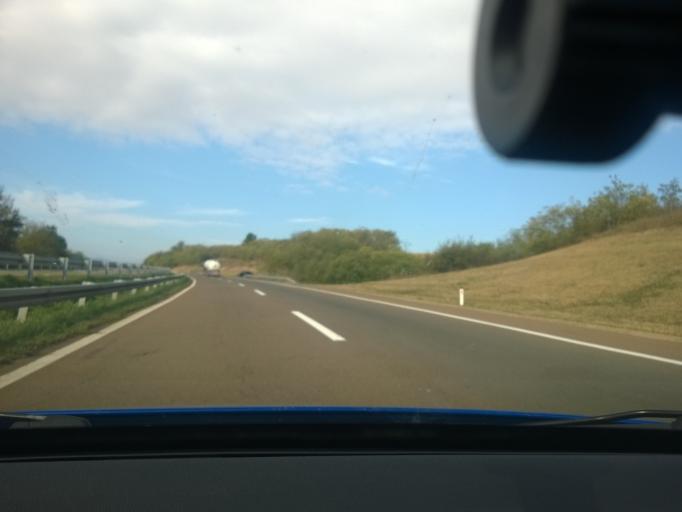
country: RS
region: Central Serbia
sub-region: Nisavski Okrug
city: Aleksinac
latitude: 43.5763
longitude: 21.6685
